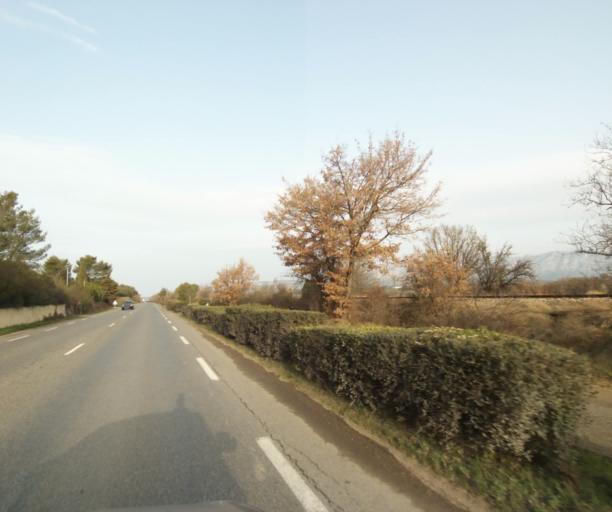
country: FR
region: Provence-Alpes-Cote d'Azur
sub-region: Departement des Bouches-du-Rhone
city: Peynier
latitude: 43.4559
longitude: 5.6622
